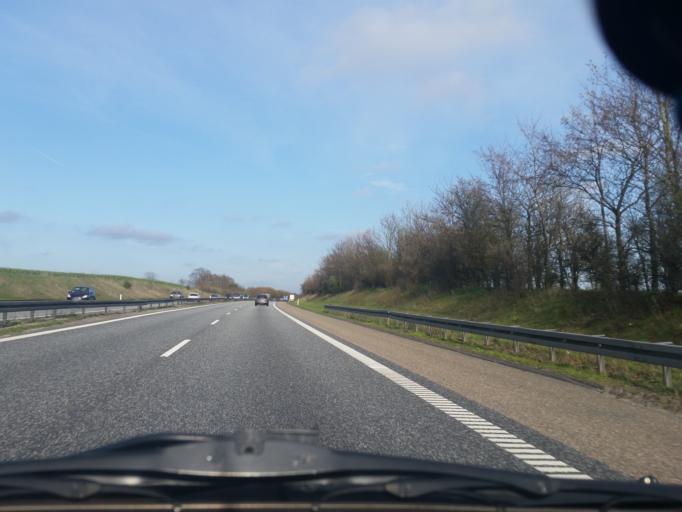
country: DK
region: Zealand
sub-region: Ringsted Kommune
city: Ringsted
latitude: 55.4526
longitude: 11.7133
